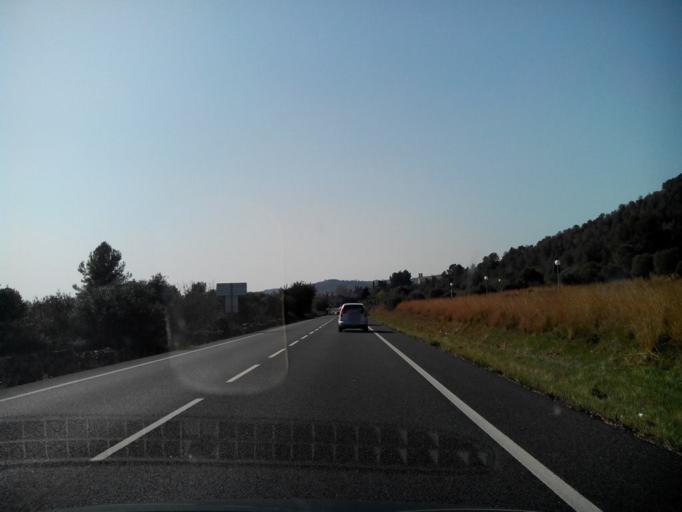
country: ES
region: Catalonia
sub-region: Provincia de Tarragona
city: Alcover
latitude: 41.2735
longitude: 1.1777
